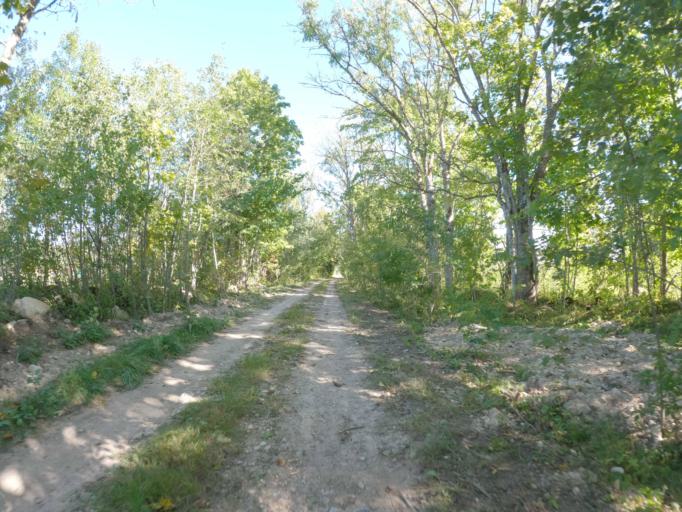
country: EE
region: Raplamaa
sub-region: Rapla vald
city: Rapla
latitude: 58.9876
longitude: 24.8115
